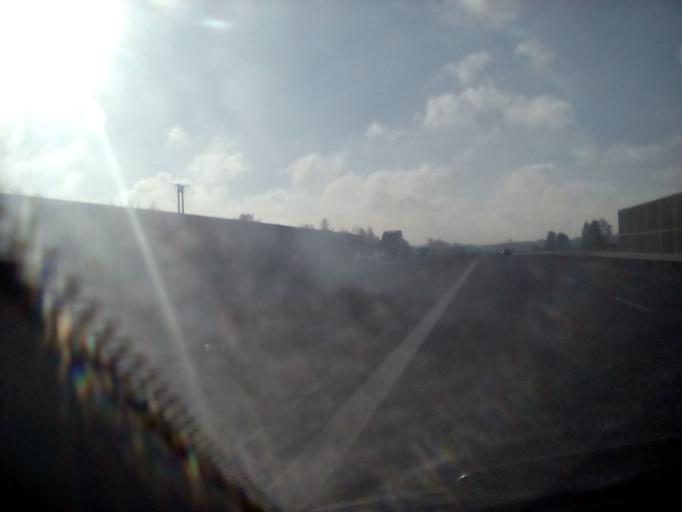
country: PL
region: Masovian Voivodeship
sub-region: Powiat grojecki
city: Grojec
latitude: 51.8125
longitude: 20.8849
